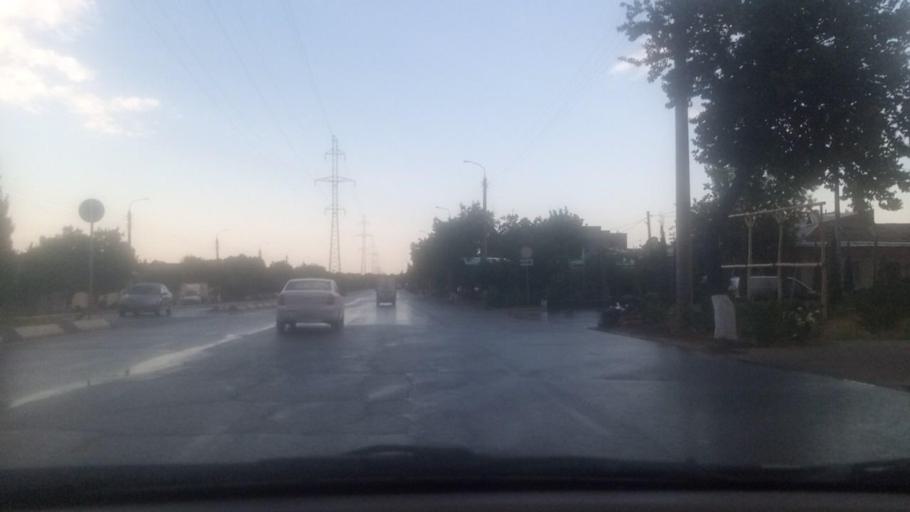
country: UZ
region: Toshkent Shahri
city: Tashkent
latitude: 41.3151
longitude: 69.1932
